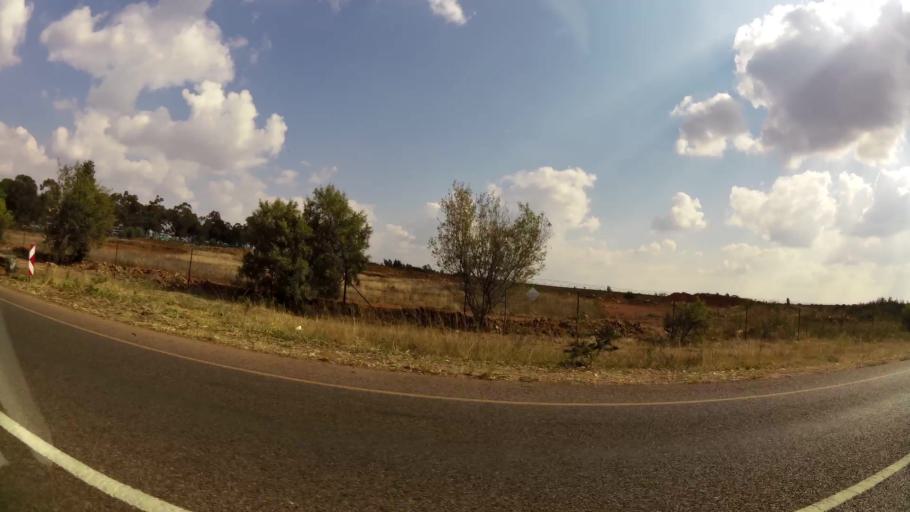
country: ZA
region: Gauteng
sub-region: City of Tshwane Metropolitan Municipality
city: Centurion
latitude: -25.8235
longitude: 28.2366
